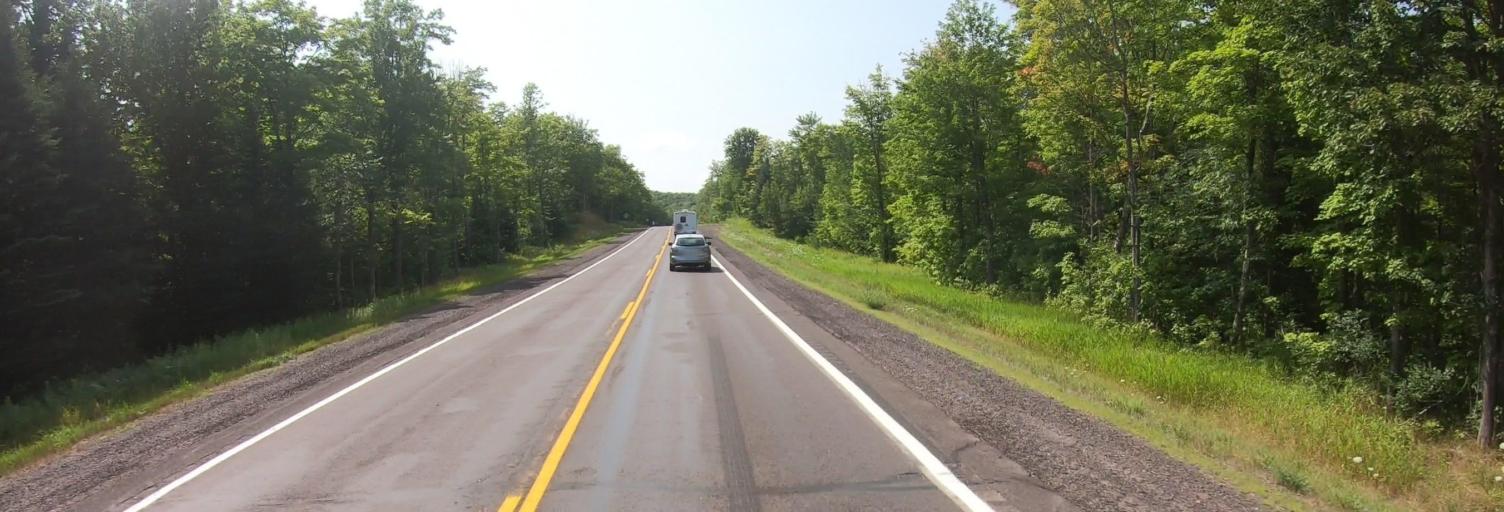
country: US
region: Michigan
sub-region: Ontonagon County
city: Ontonagon
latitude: 46.8576
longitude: -88.9280
